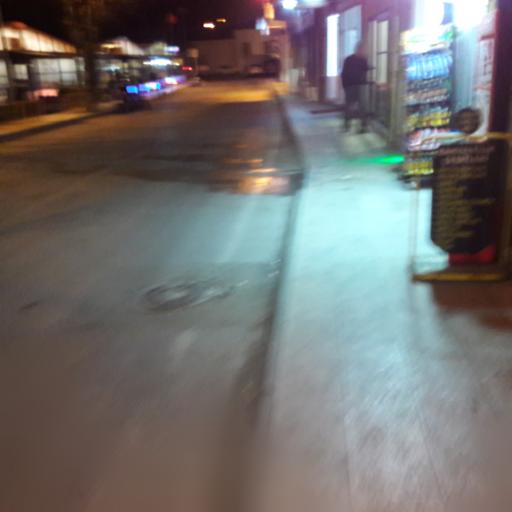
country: TR
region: Sinop
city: Sinop
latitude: 42.0246
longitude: 35.1481
